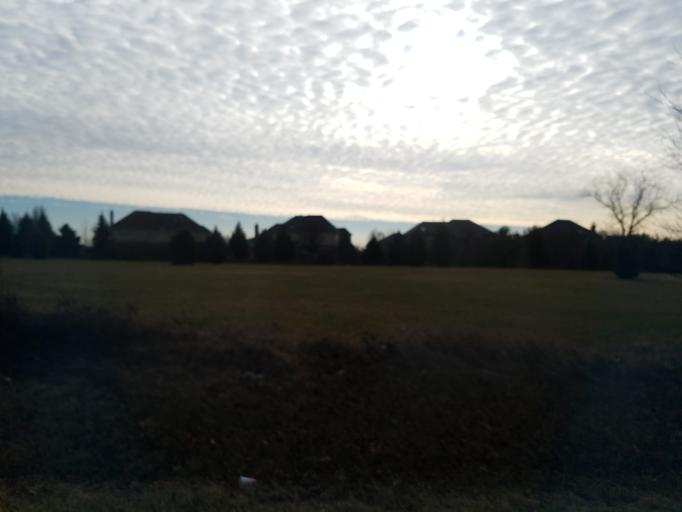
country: US
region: Illinois
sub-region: Will County
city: Mokena
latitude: 41.5283
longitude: -87.9061
